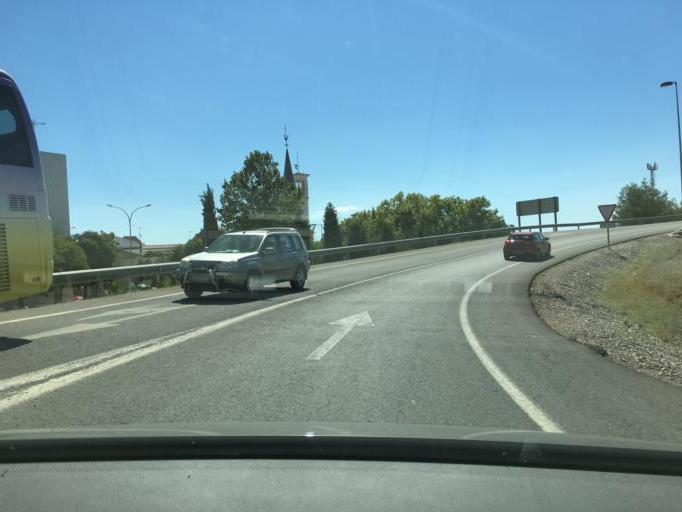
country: ES
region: Andalusia
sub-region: Provincia de Granada
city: Albolote
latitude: 37.2587
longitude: -3.6579
